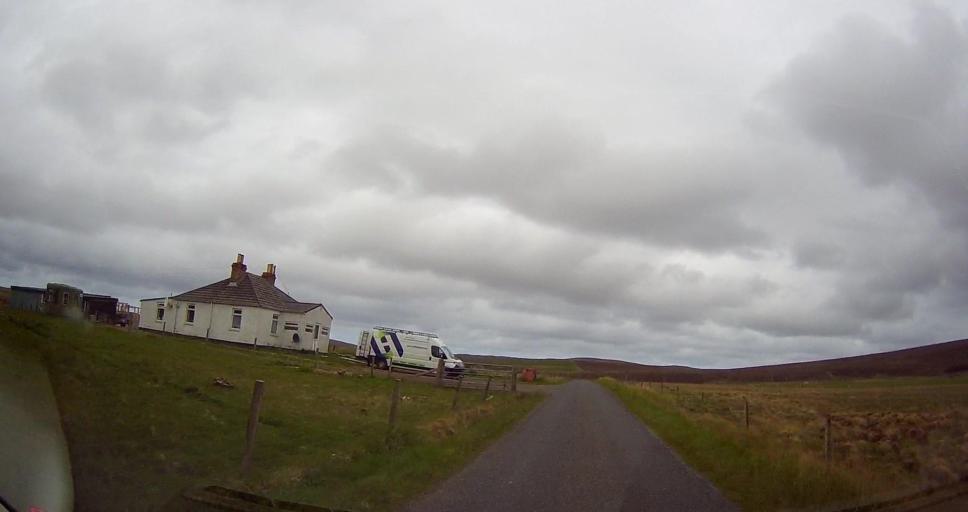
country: GB
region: Scotland
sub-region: Shetland Islands
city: Shetland
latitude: 60.7909
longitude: -0.8458
